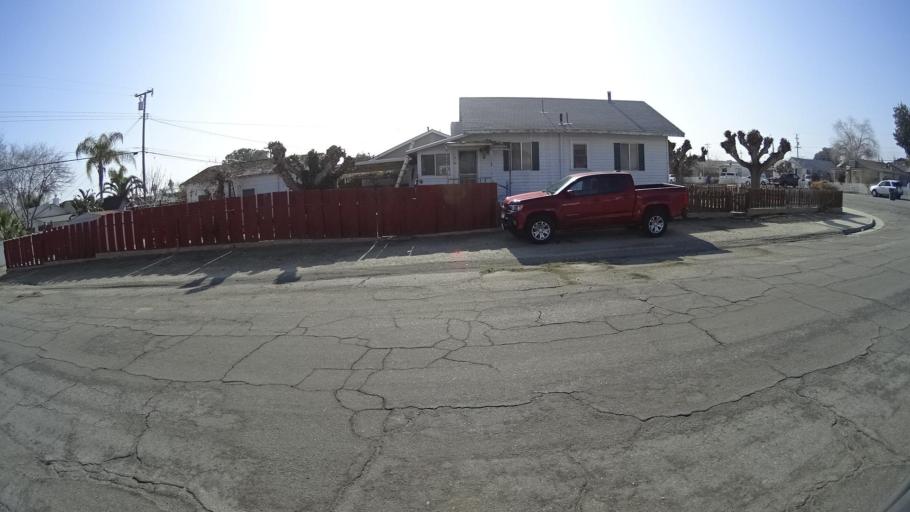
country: US
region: California
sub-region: Kern County
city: Ford City
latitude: 35.1561
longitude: -119.4622
